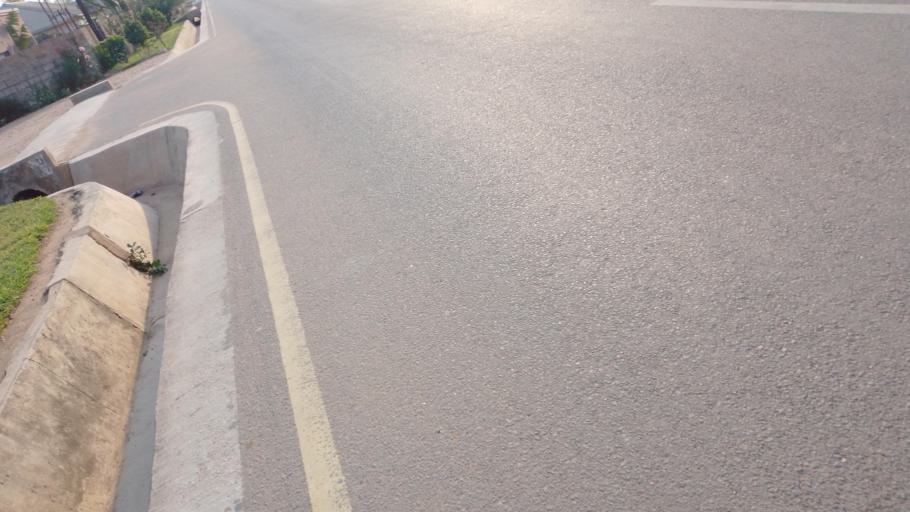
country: ZM
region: Lusaka
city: Lusaka
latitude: -15.3993
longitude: 28.3865
